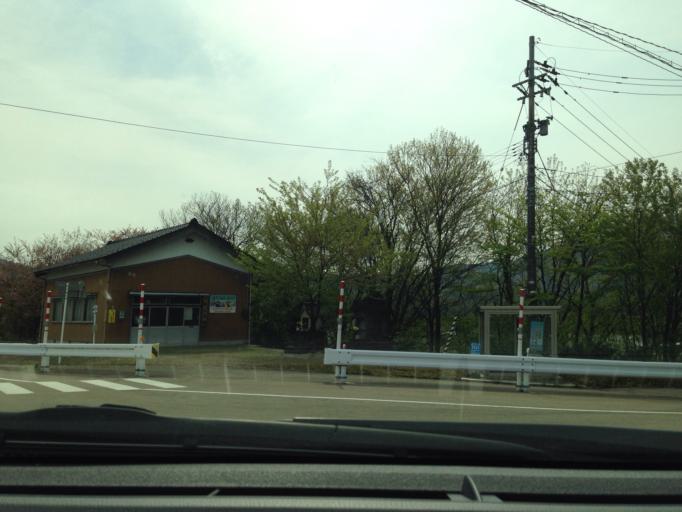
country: JP
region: Toyama
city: Fukumitsu
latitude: 36.5178
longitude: 136.8573
